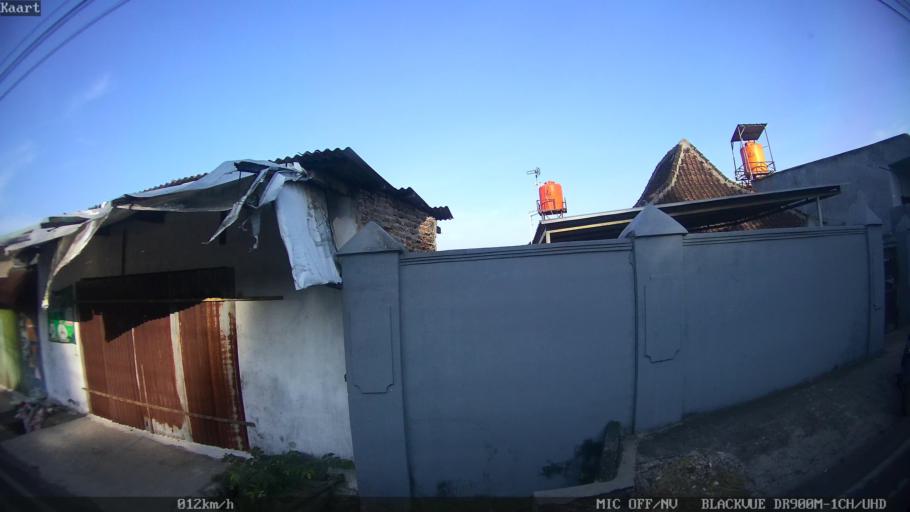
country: ID
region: Lampung
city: Bandarlampung
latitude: -5.4072
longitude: 105.2490
